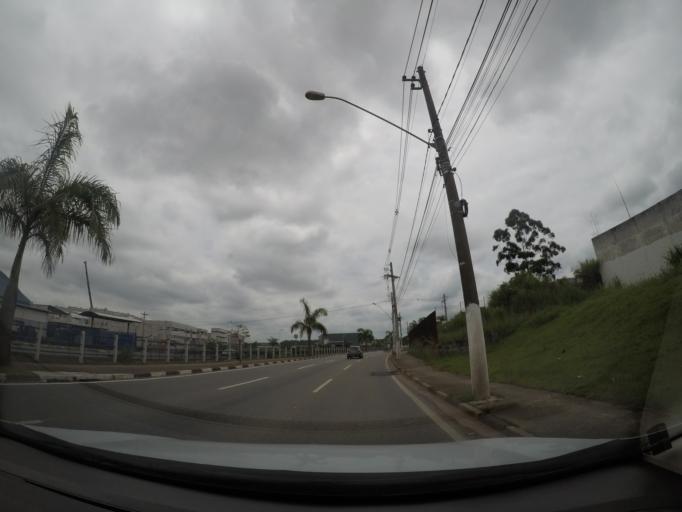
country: BR
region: Sao Paulo
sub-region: Aruja
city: Aruja
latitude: -23.4018
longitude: -46.3505
